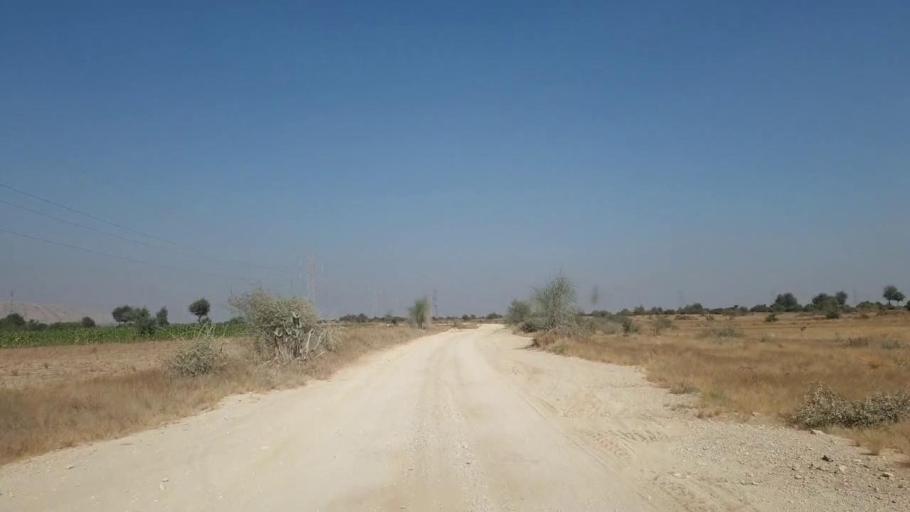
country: PK
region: Sindh
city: Thatta
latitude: 25.2503
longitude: 67.8056
